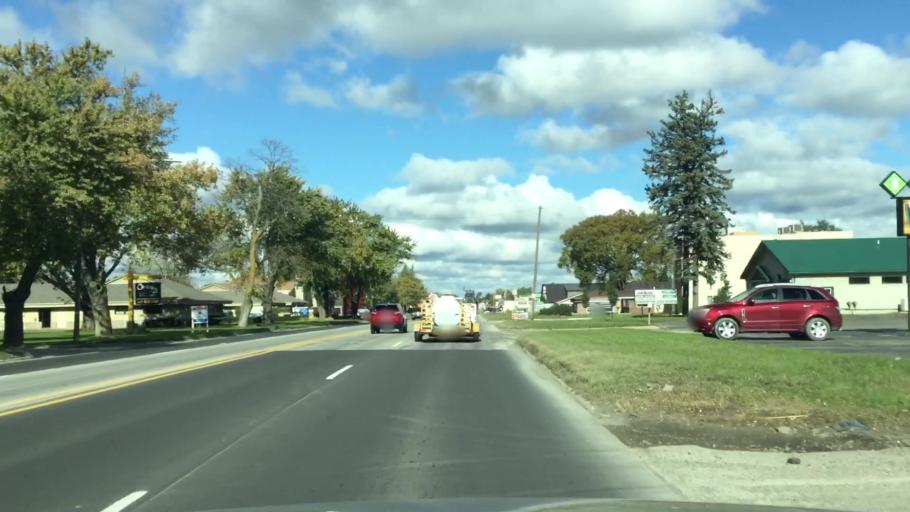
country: US
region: Michigan
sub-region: Oakland County
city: Oxford
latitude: 42.8122
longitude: -83.2534
